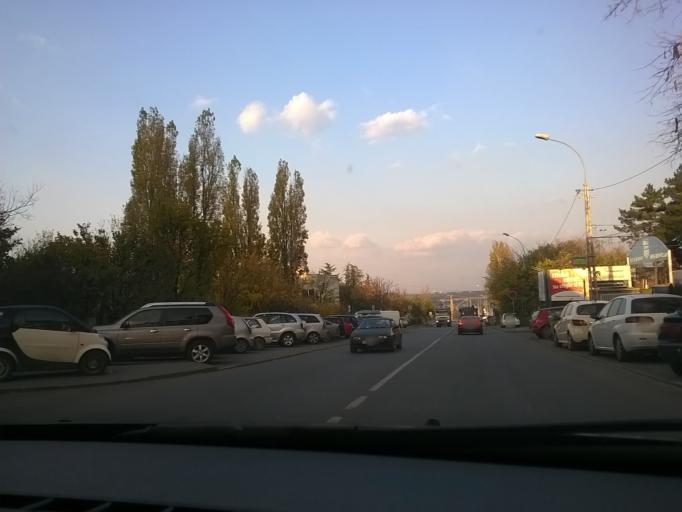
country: RS
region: Central Serbia
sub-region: Belgrade
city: Palilula
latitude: 44.8161
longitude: 20.4927
